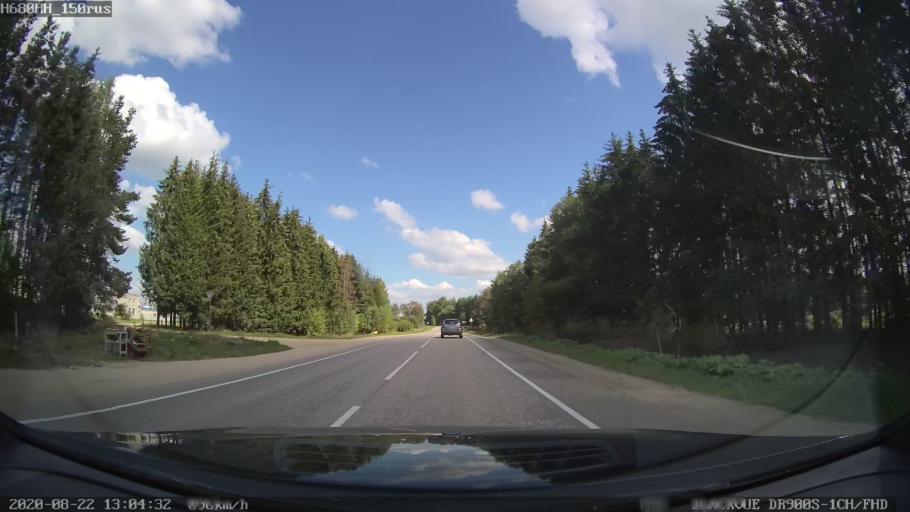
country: RU
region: Tverskaya
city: Bezhetsk
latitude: 57.6669
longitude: 36.4328
